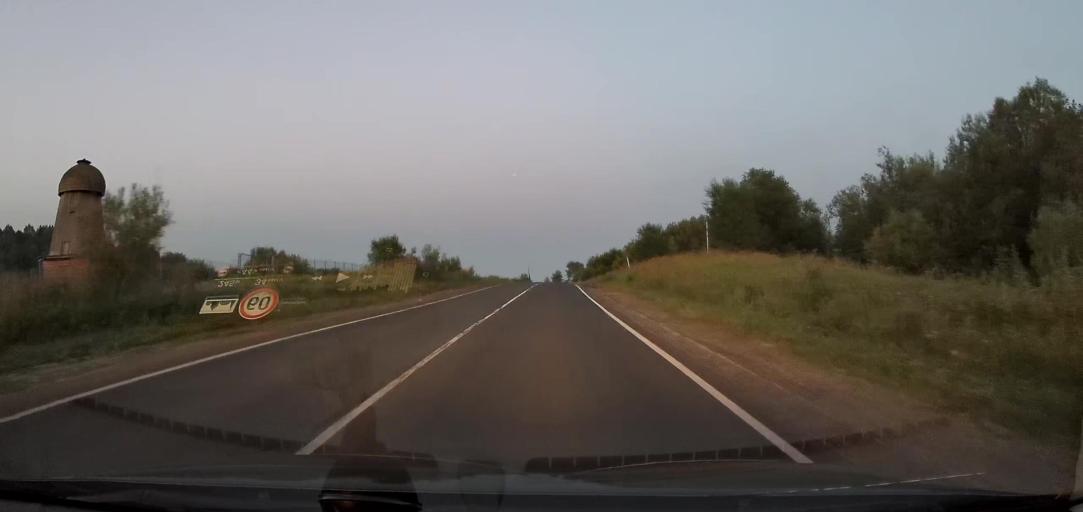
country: RU
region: Arkhangelskaya
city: Uyemskiy
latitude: 64.4494
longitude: 40.9444
